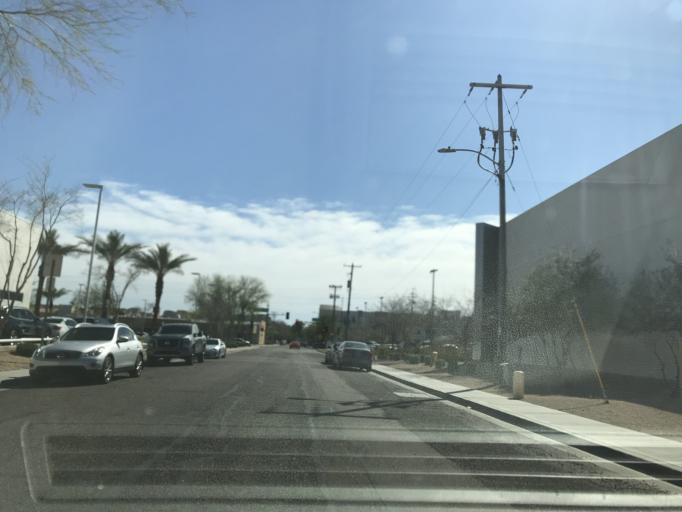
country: US
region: Arizona
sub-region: Maricopa County
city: Phoenix
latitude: 33.5104
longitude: -112.0628
